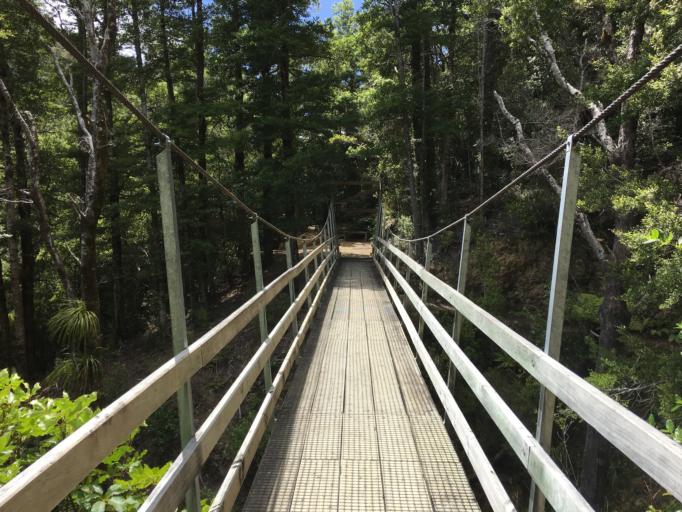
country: NZ
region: Wellington
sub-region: Lower Hutt City
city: Lower Hutt
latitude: -41.3420
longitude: 174.9497
